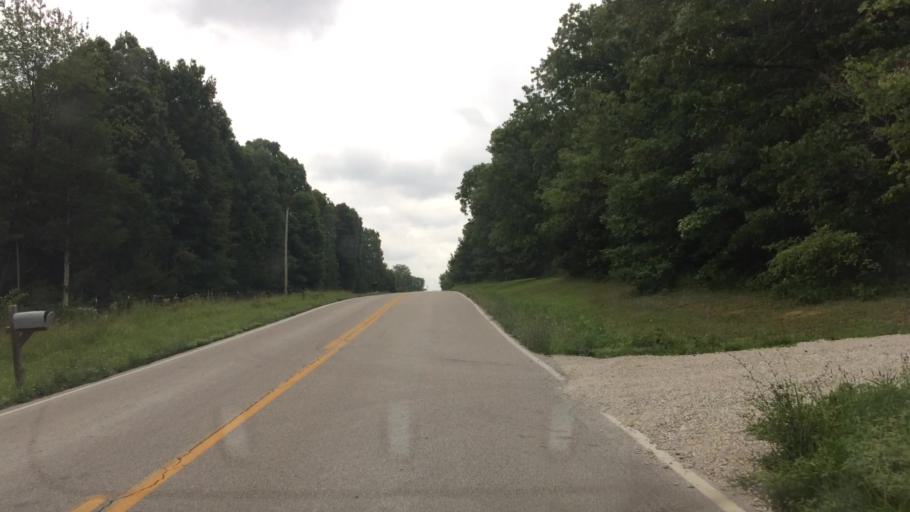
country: US
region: Missouri
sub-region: Webster County
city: Marshfield
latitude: 37.3415
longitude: -93.0103
